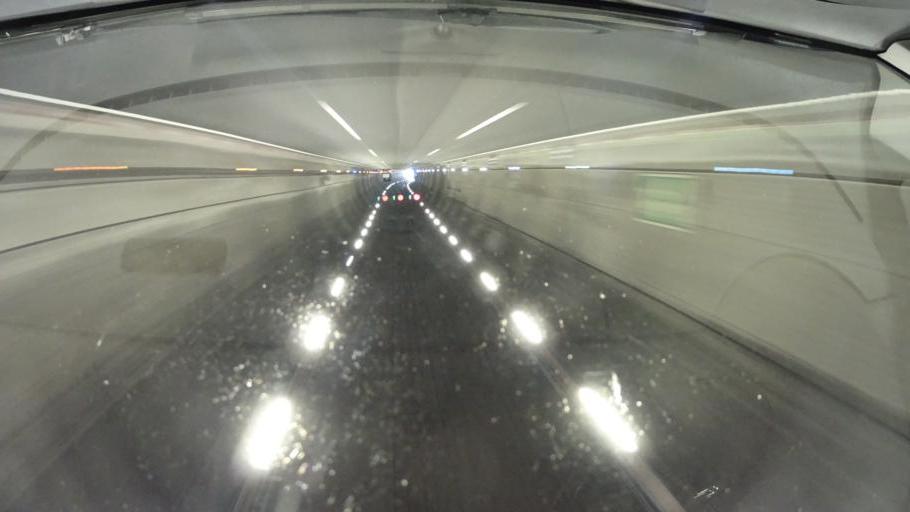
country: ES
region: Madrid
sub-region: Provincia de Madrid
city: Somosierra
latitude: 41.1340
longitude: -3.5831
